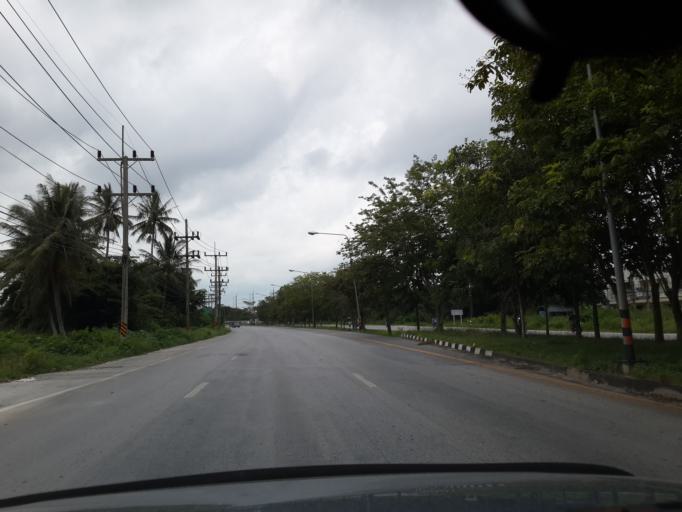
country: TH
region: Pattani
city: Pattani
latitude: 6.8698
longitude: 101.2792
